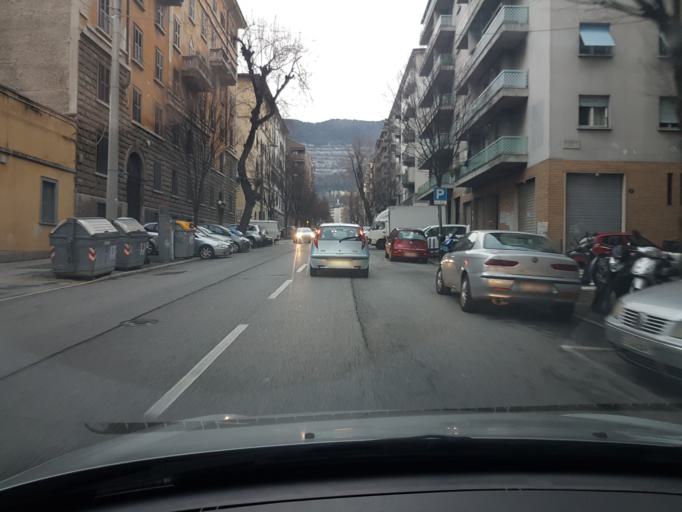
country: IT
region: Friuli Venezia Giulia
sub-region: Provincia di Trieste
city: Trieste
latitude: 45.6552
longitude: 13.8000
